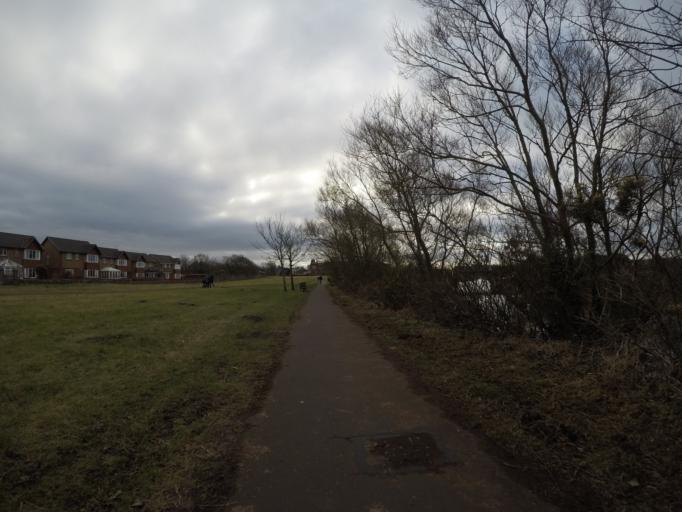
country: GB
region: Scotland
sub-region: North Ayrshire
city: Irvine
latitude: 55.6208
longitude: -4.6737
